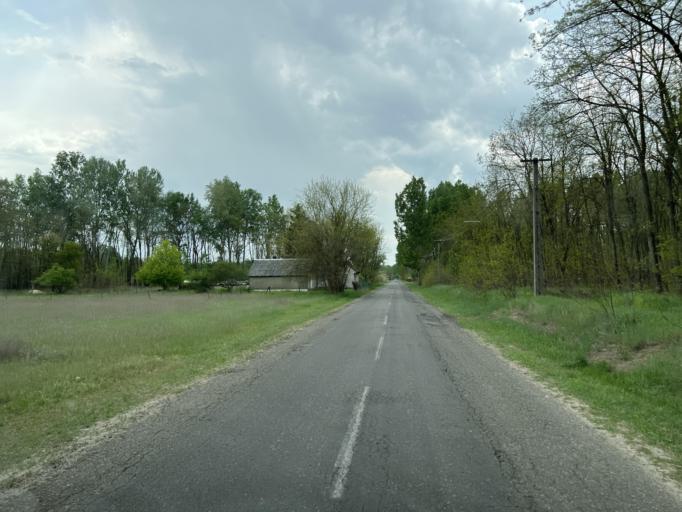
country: HU
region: Pest
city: Csemo
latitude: 47.1070
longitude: 19.7357
